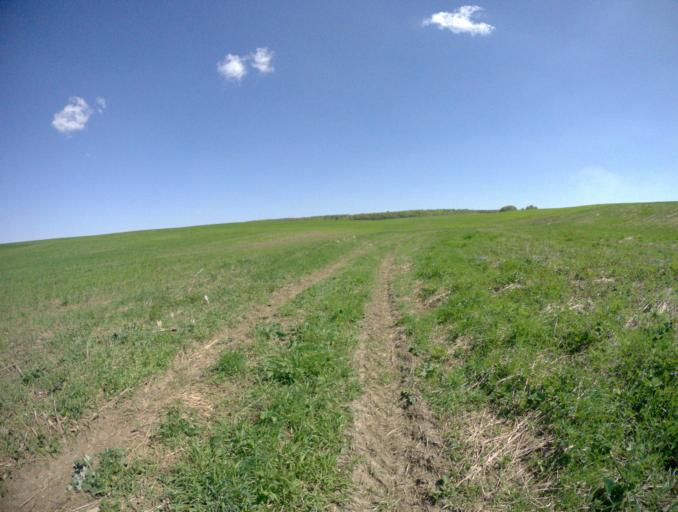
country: RU
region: Vladimir
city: Suzdal'
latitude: 56.2930
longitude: 40.3813
